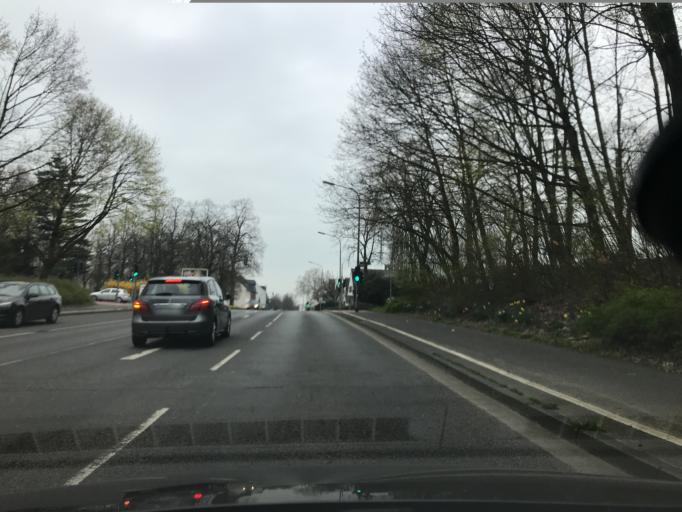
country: DE
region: North Rhine-Westphalia
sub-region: Regierungsbezirk Dusseldorf
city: Viersen
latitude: 51.2578
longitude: 6.3316
